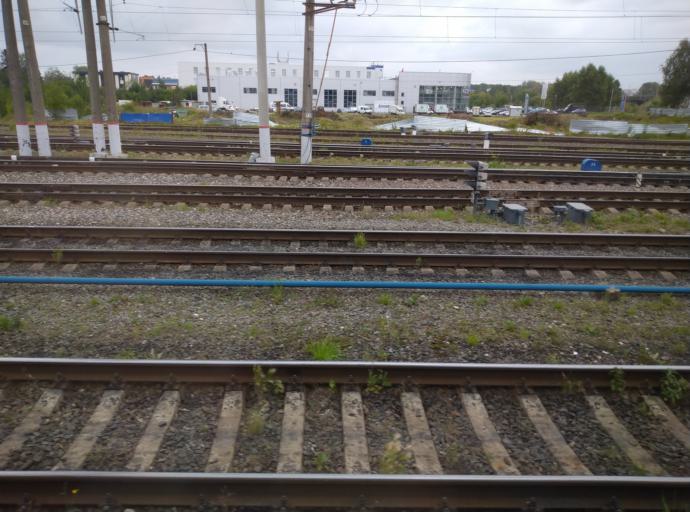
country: RU
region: Kostroma
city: Oktyabr'skiy
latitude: 57.7575
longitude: 40.9799
